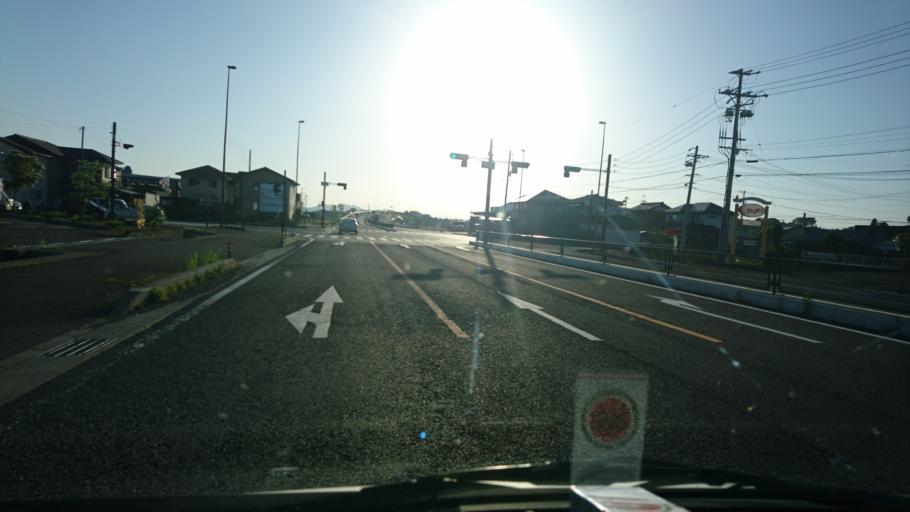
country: JP
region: Gifu
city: Mitake
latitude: 35.4303
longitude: 137.0877
